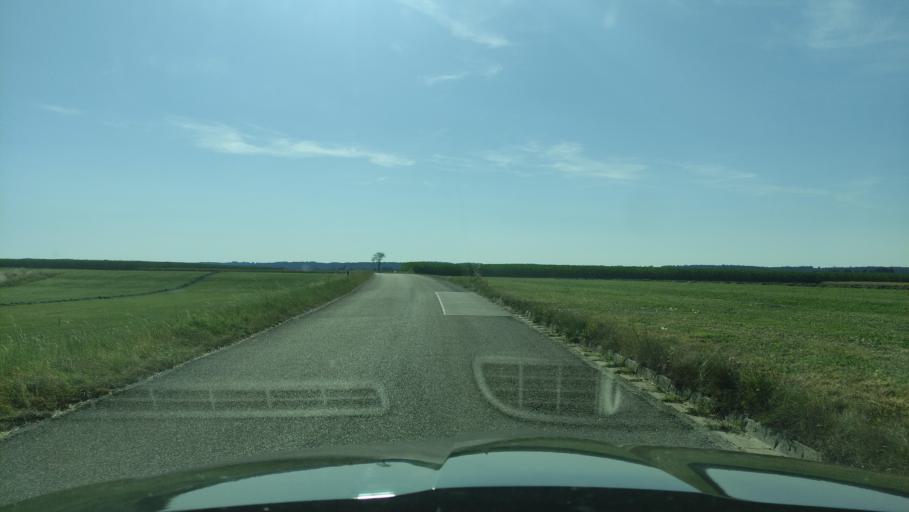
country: DE
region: Bavaria
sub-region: Swabia
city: Ebershausen
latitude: 48.2074
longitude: 10.3099
